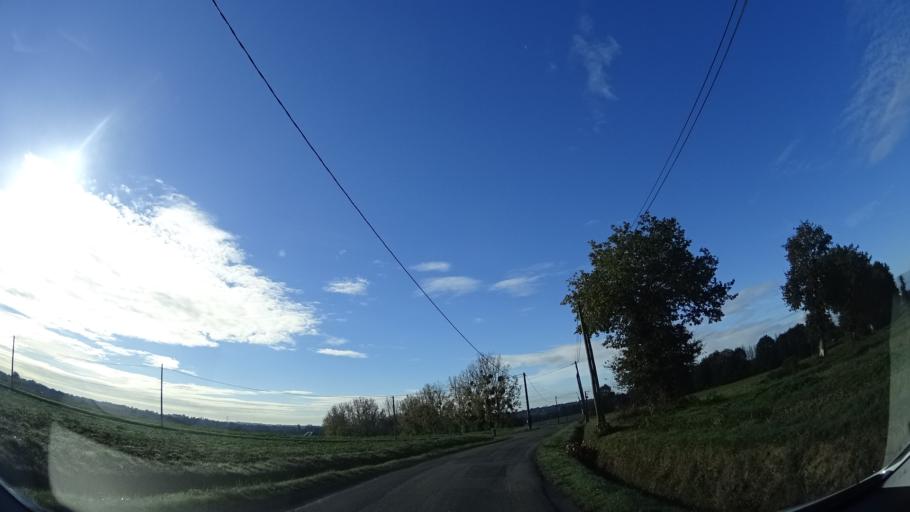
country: FR
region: Brittany
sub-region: Departement d'Ille-et-Vilaine
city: Geveze
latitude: 48.2068
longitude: -1.7744
